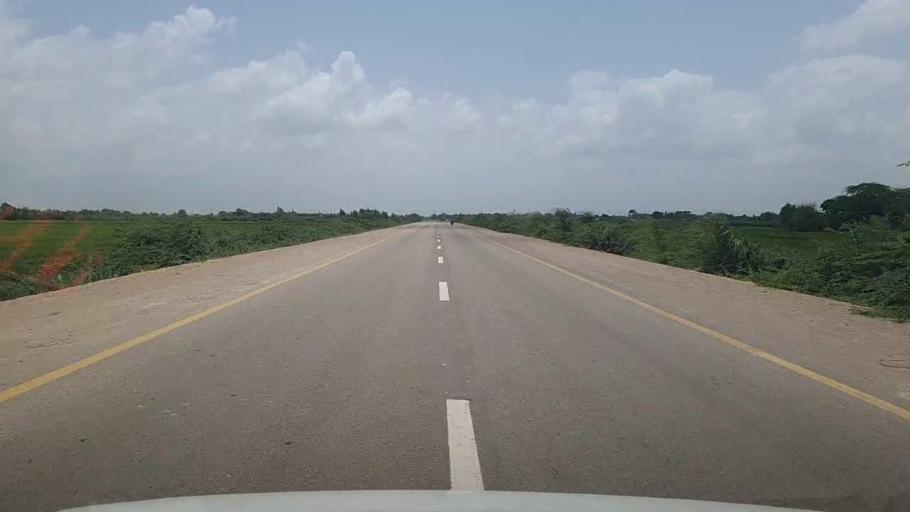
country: PK
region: Sindh
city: Thatta
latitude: 24.7560
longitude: 67.9526
